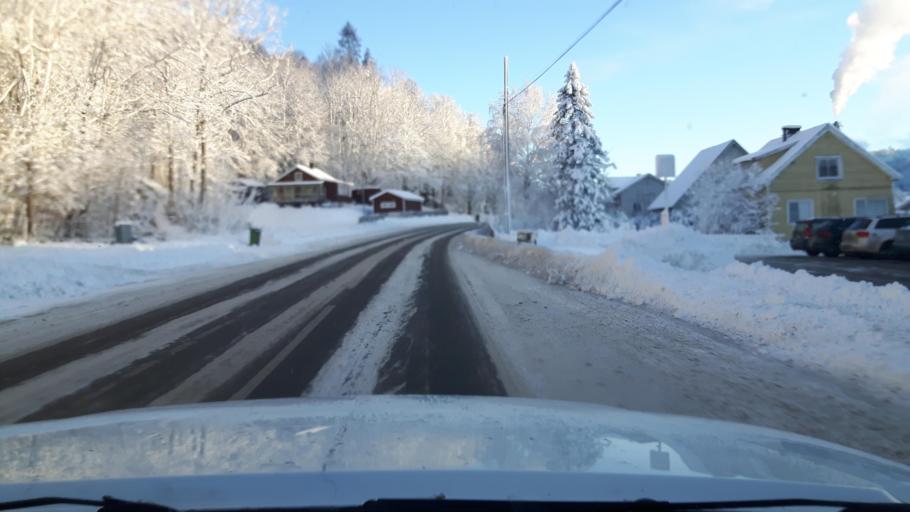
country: SE
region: Halland
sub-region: Kungsbacka Kommun
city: Fjaeras kyrkby
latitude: 57.5461
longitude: 12.1729
